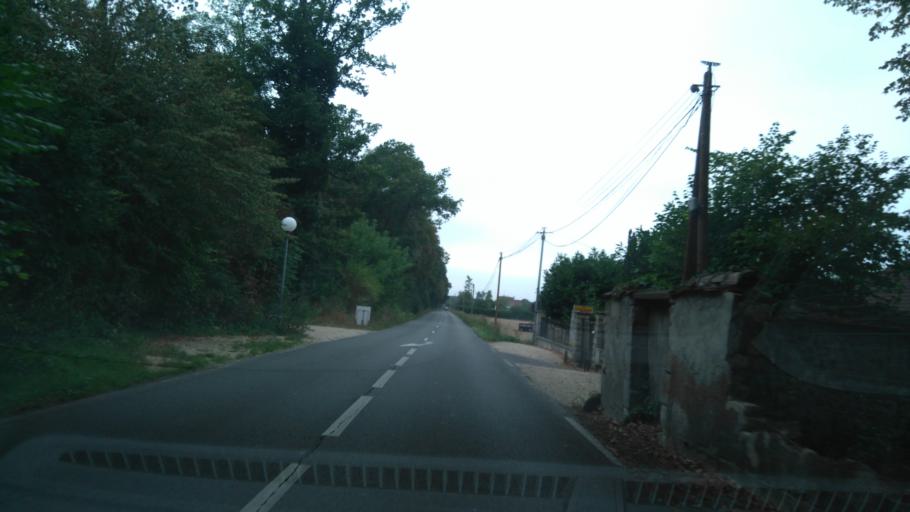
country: FR
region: Picardie
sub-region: Departement de l'Oise
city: Gouvieux
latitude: 49.1878
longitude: 2.4014
